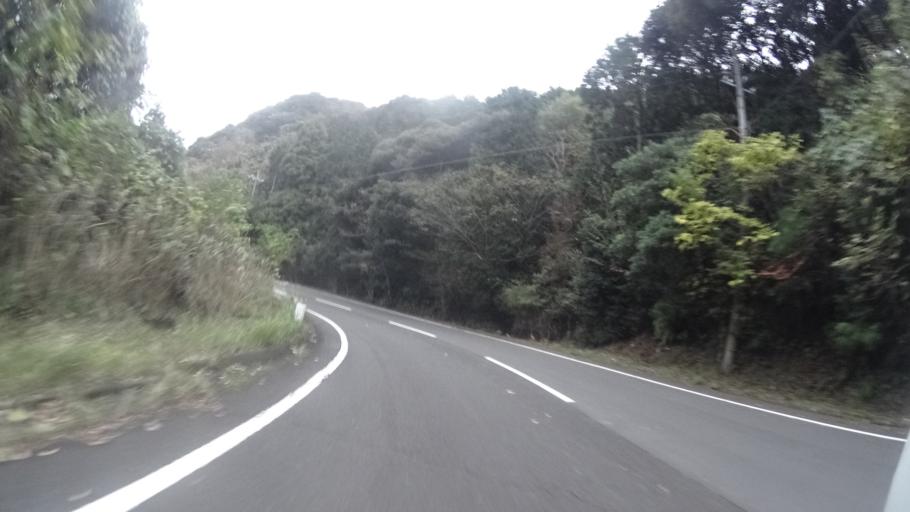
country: JP
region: Kyoto
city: Maizuru
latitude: 35.5691
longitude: 135.4507
